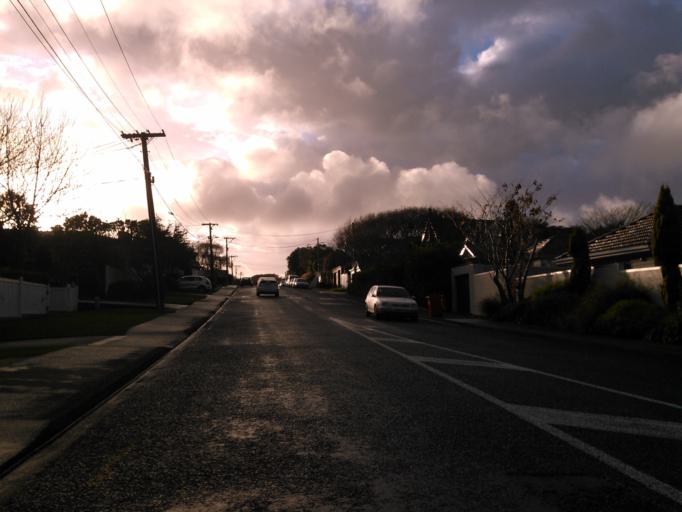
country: NZ
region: Wellington
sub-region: Wellington City
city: Kelburn
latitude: -41.2819
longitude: 174.7396
